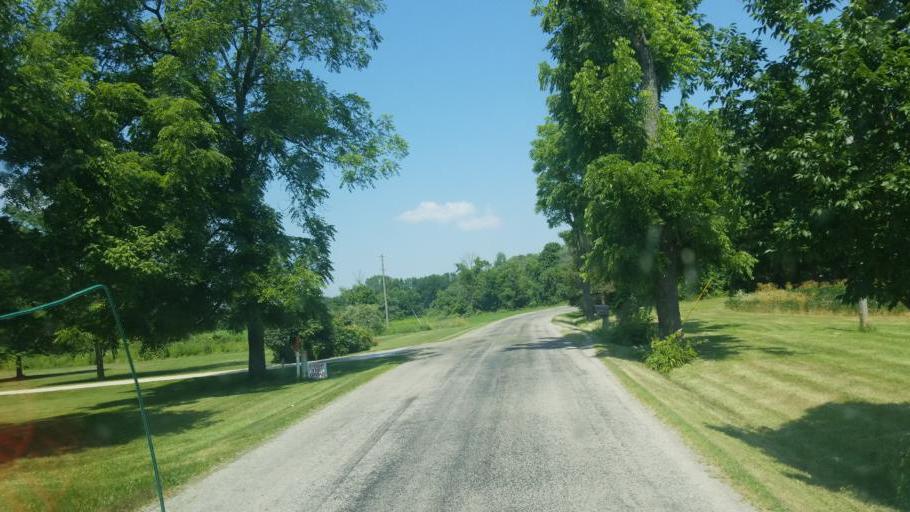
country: US
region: Ohio
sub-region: Richland County
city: Shelby
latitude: 40.8309
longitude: -82.6415
